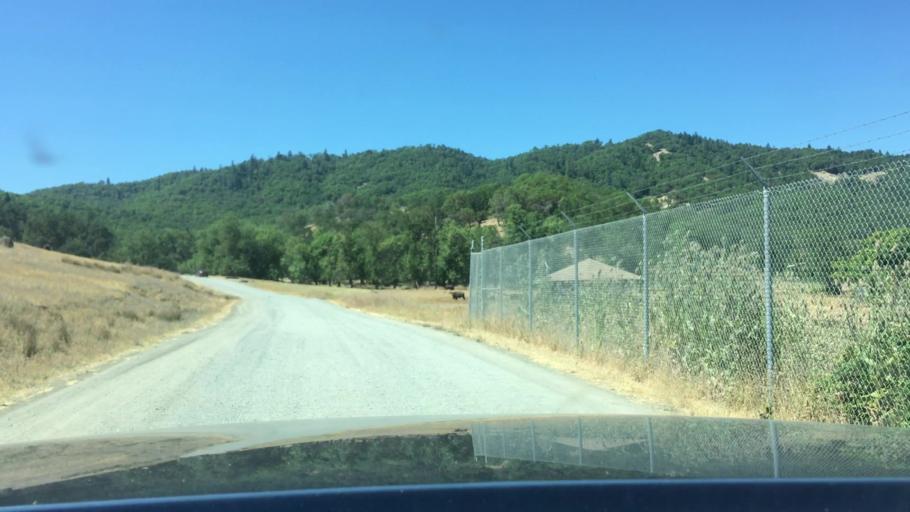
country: US
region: Oregon
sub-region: Douglas County
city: Winston
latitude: 43.1306
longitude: -123.4349
